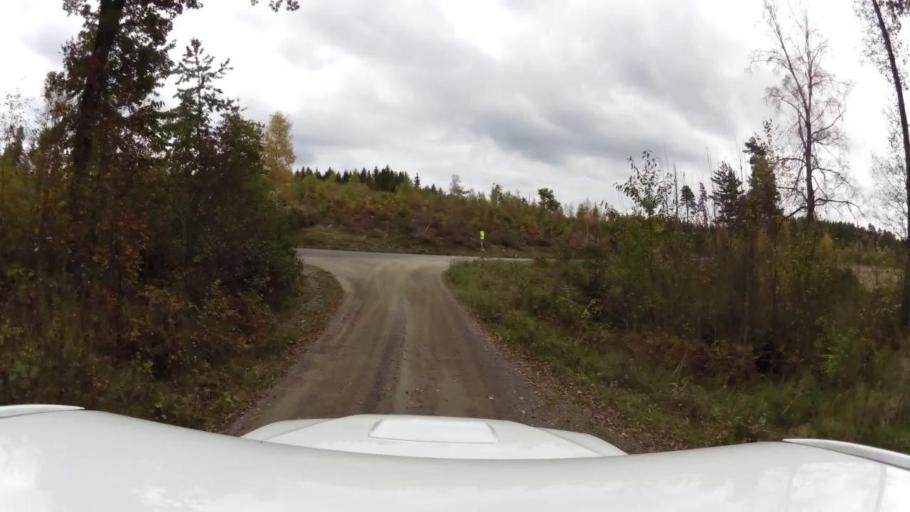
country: SE
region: OEstergoetland
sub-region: Linkopings Kommun
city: Ljungsbro
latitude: 58.5425
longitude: 15.4461
